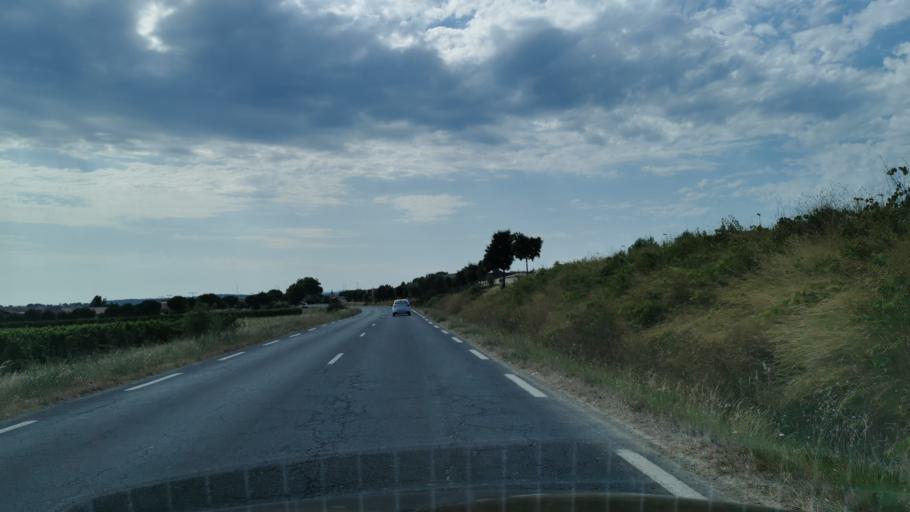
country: FR
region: Languedoc-Roussillon
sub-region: Departement de l'Herault
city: Puisserguier
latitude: 43.3662
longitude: 3.0563
